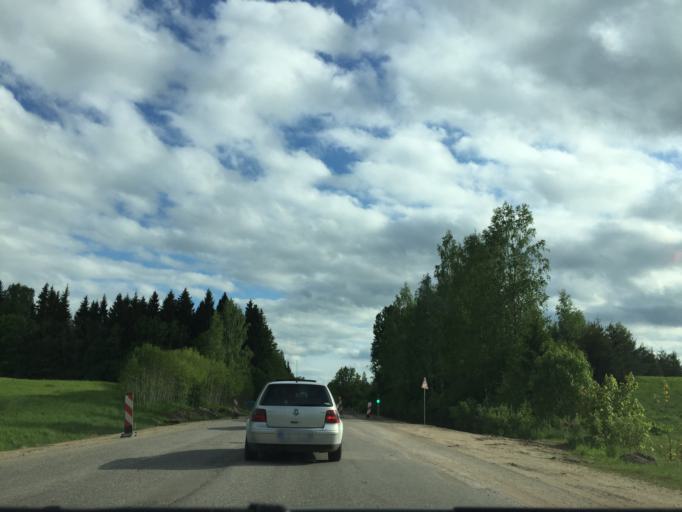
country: LV
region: Amatas Novads
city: Drabesi
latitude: 57.2535
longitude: 25.2629
